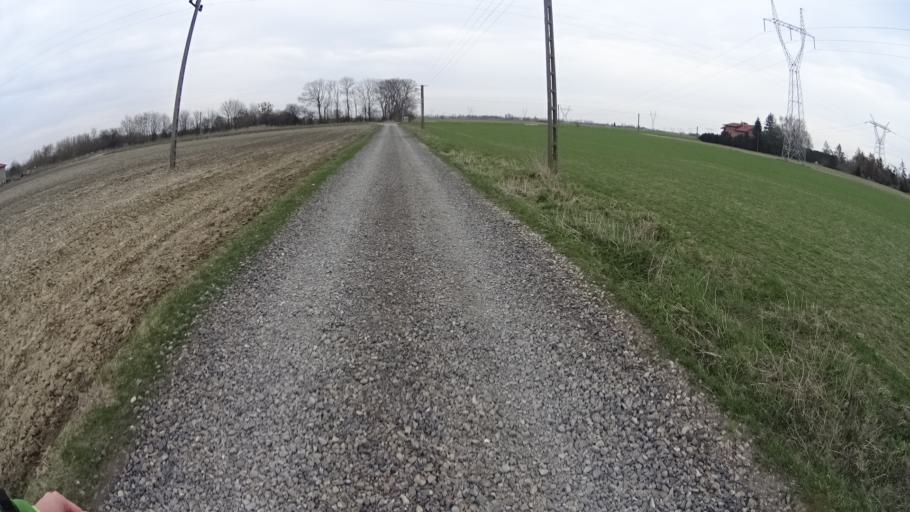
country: PL
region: Masovian Voivodeship
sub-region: Powiat warszawski zachodni
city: Jozefow
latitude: 52.2396
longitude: 20.6903
